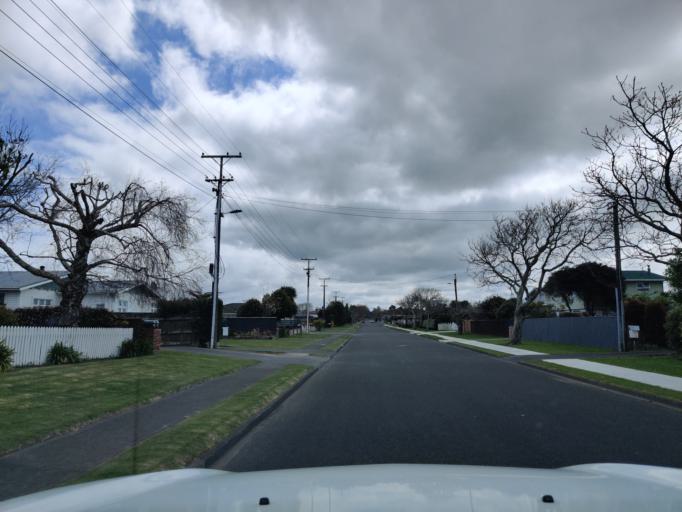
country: NZ
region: Manawatu-Wanganui
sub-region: Wanganui District
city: Wanganui
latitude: -39.9276
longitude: 175.0276
